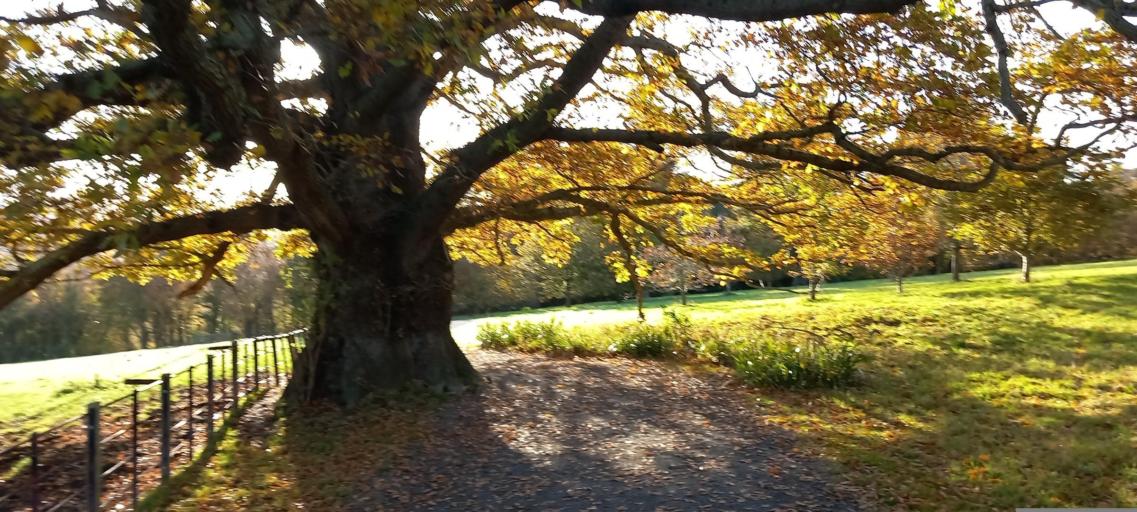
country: GB
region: Wales
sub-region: Anglesey
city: Beaumaris
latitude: 53.2259
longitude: -4.0928
